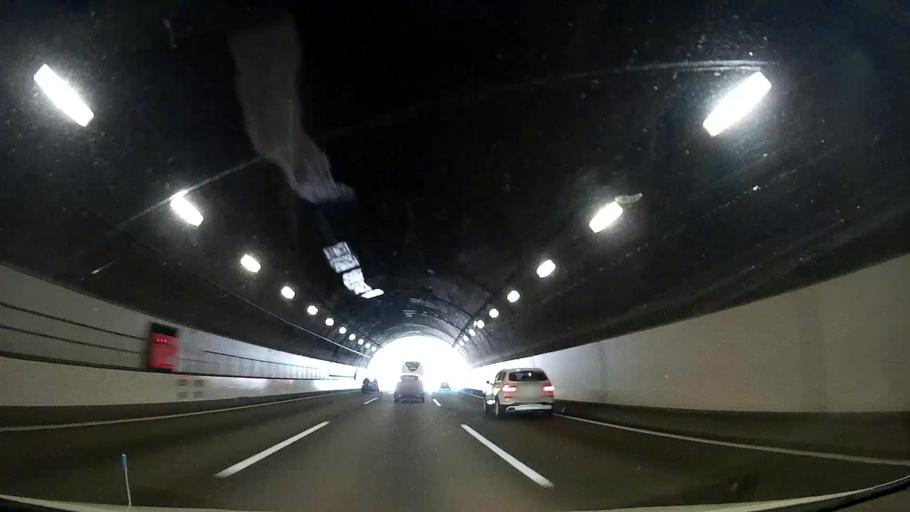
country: JP
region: Shizuoka
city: Gotemba
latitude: 35.3537
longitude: 138.9945
